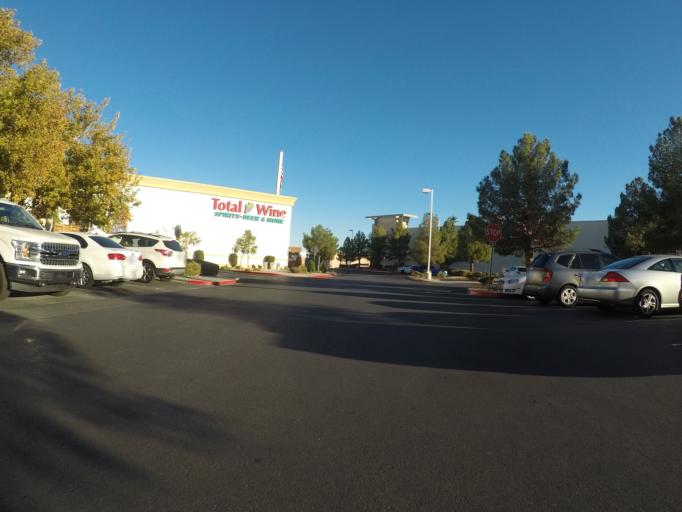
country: US
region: Nevada
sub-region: Clark County
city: Summerlin South
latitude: 36.1630
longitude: -115.2893
